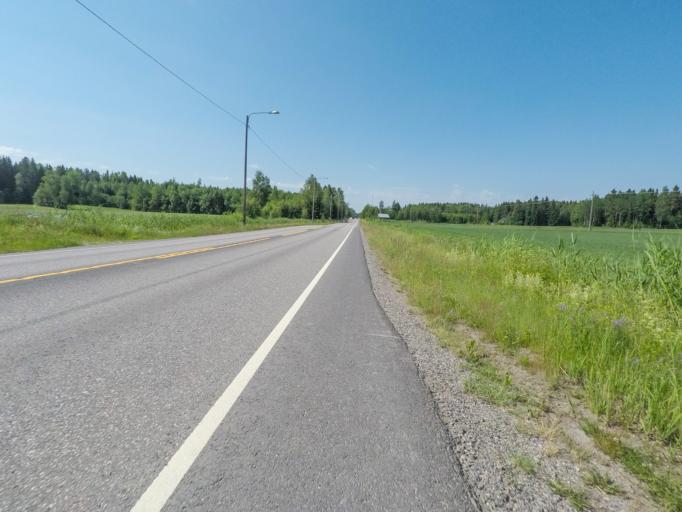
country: FI
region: Uusimaa
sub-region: Helsinki
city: Nickby
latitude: 60.3216
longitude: 25.4180
